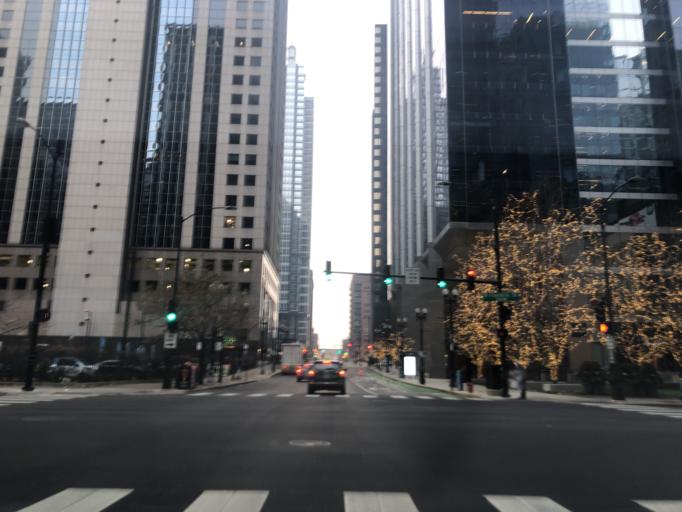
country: US
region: Illinois
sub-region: Cook County
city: Chicago
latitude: 41.8845
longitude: -87.6352
